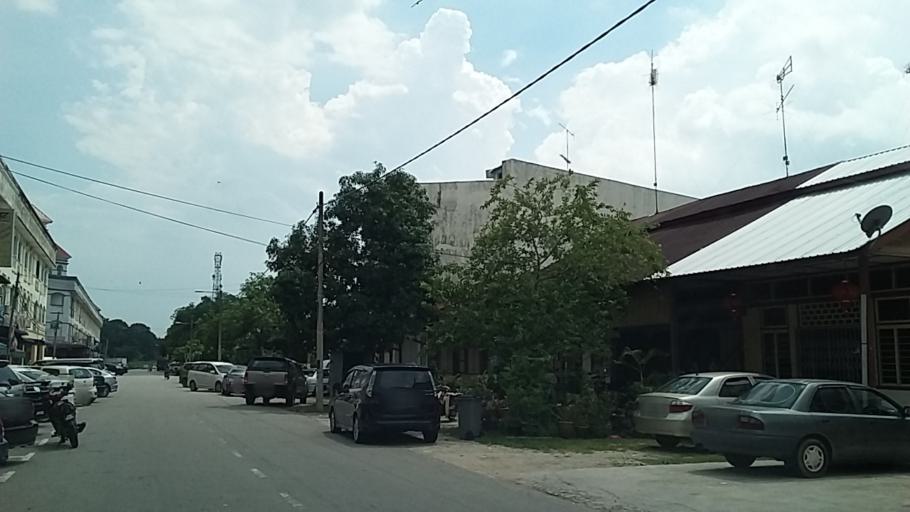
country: MY
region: Johor
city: Parit Raja
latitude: 1.7483
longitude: 103.0517
